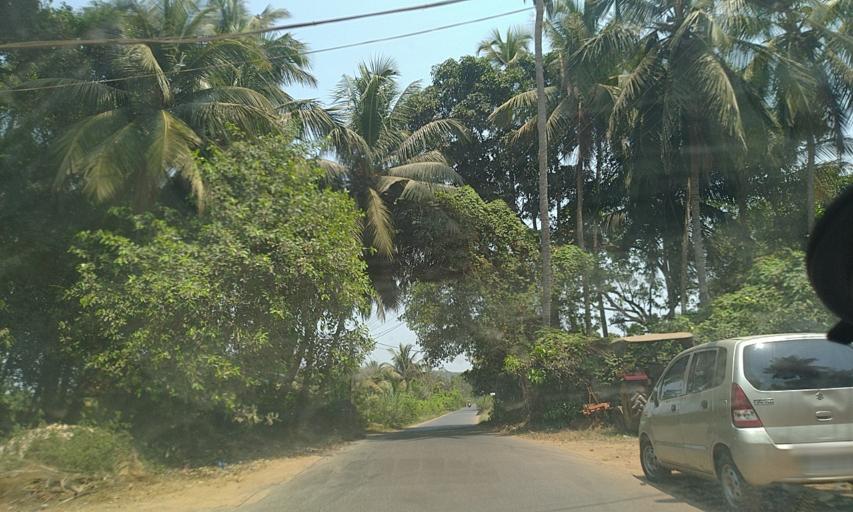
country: IN
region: Goa
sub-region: North Goa
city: Guirim
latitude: 15.5532
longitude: 73.8139
